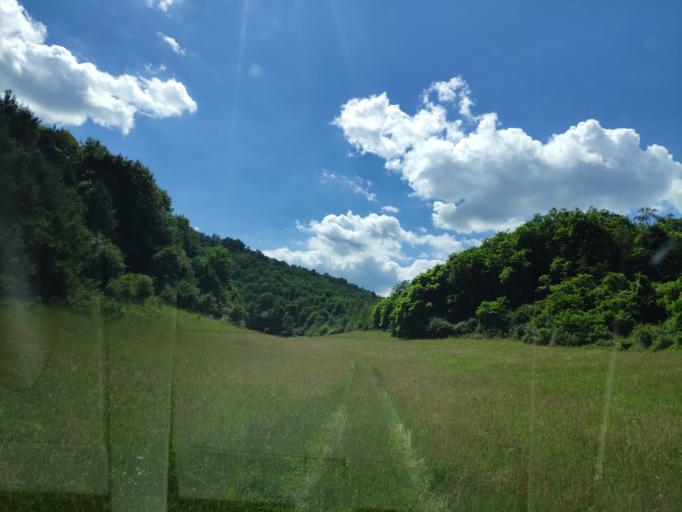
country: HU
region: Borsod-Abauj-Zemplen
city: Arlo
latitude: 48.2548
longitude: 20.1762
